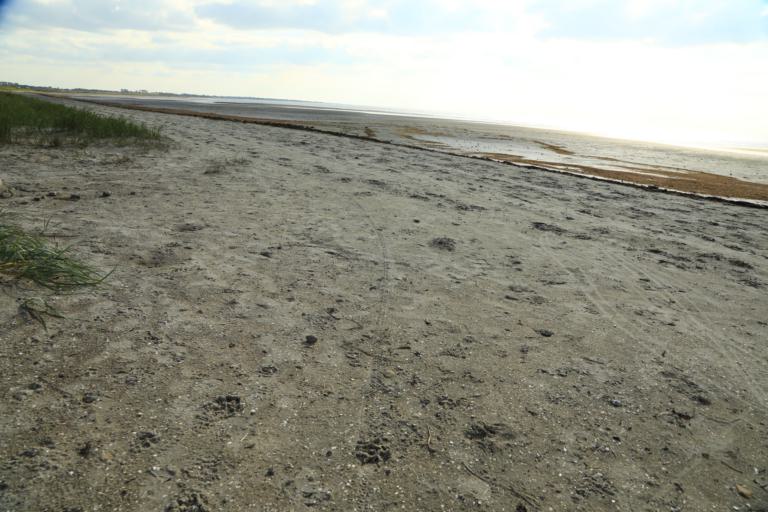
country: SE
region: Halland
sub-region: Varbergs Kommun
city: Tvaaker
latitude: 57.0090
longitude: 12.3463
